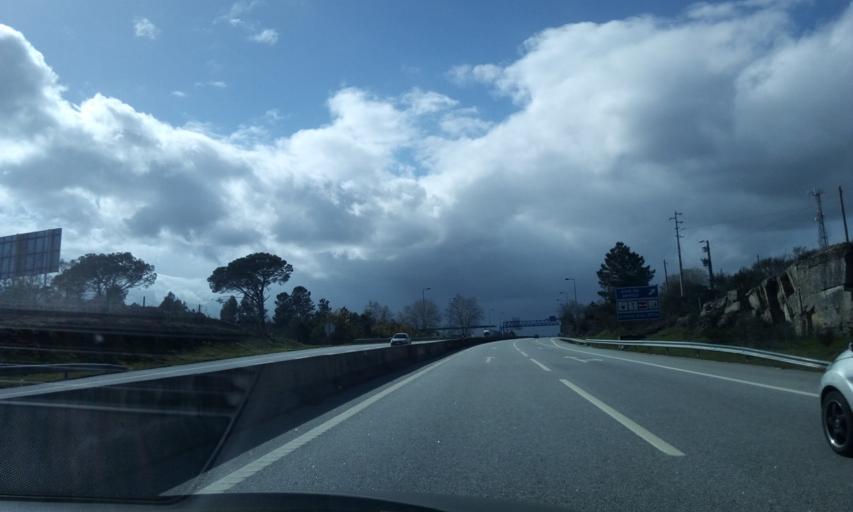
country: PT
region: Viseu
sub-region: Mangualde
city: Mangualde
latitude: 40.6247
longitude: -7.7774
